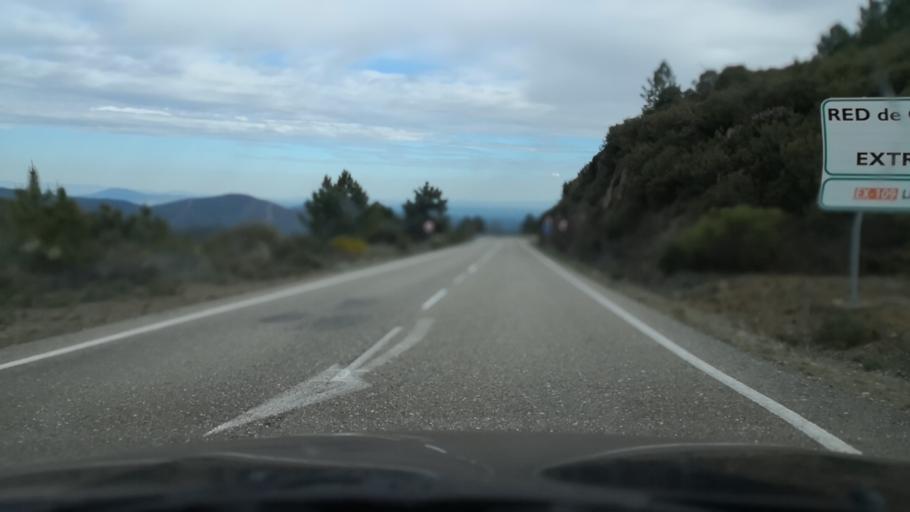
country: ES
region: Extremadura
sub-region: Provincia de Caceres
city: Acebo
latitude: 40.2456
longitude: -6.6868
